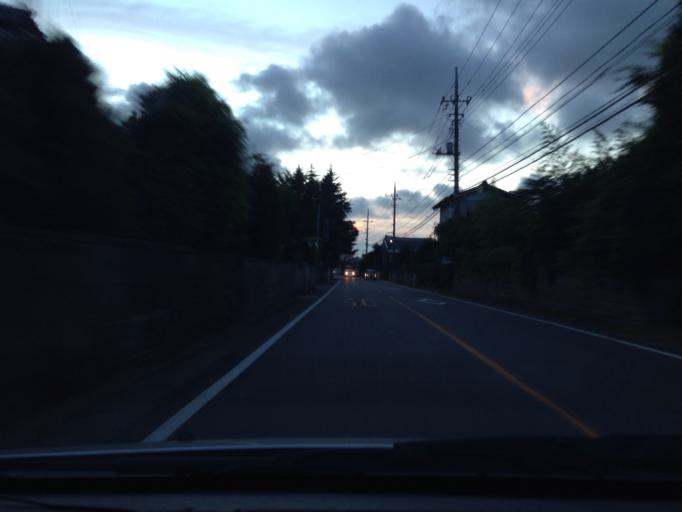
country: JP
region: Ibaraki
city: Ami
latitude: 36.0288
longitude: 140.2761
